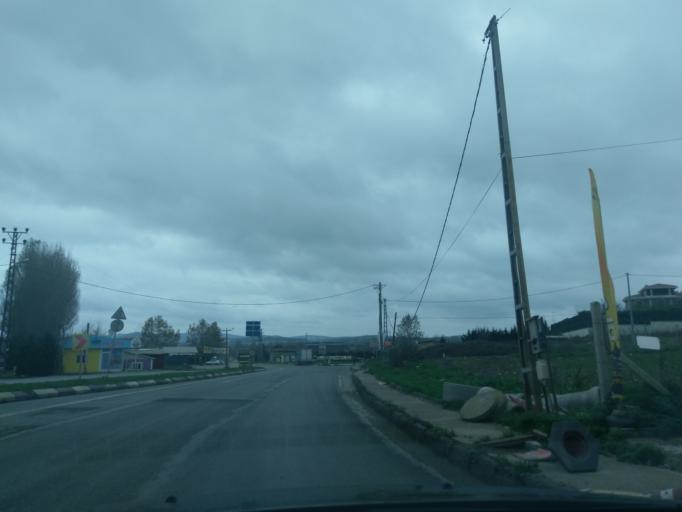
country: TR
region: Istanbul
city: Catalca
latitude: 41.1600
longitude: 28.4544
